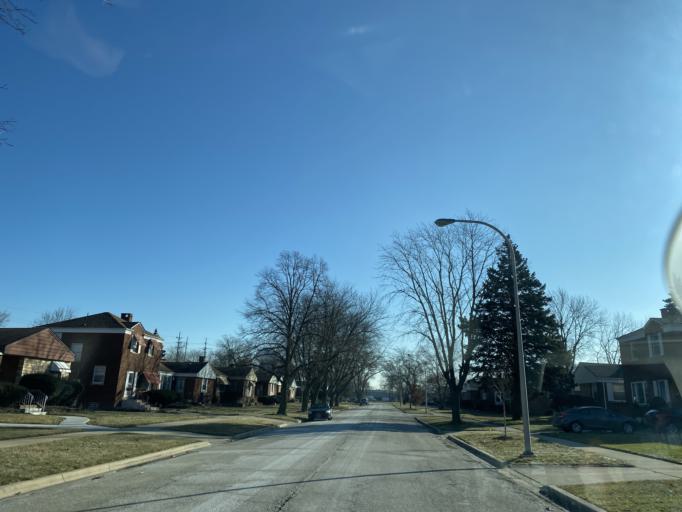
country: US
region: Illinois
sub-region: Cook County
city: Westchester
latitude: 41.8612
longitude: -87.8707
